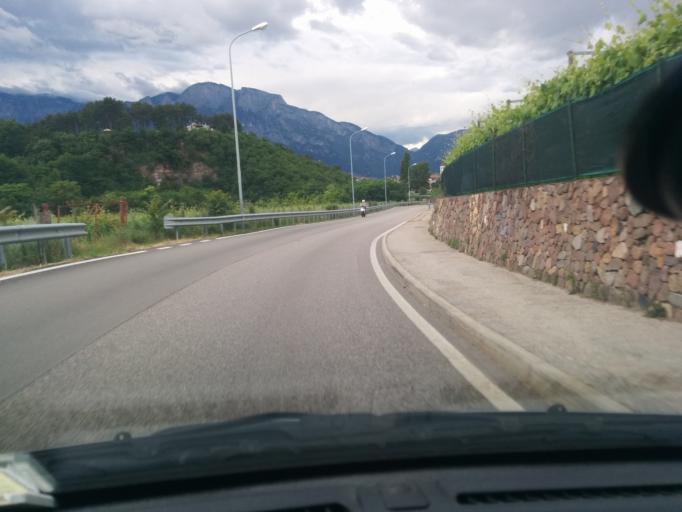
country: IT
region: Trentino-Alto Adige
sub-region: Provincia di Trento
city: Trento
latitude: 46.0836
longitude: 11.1350
